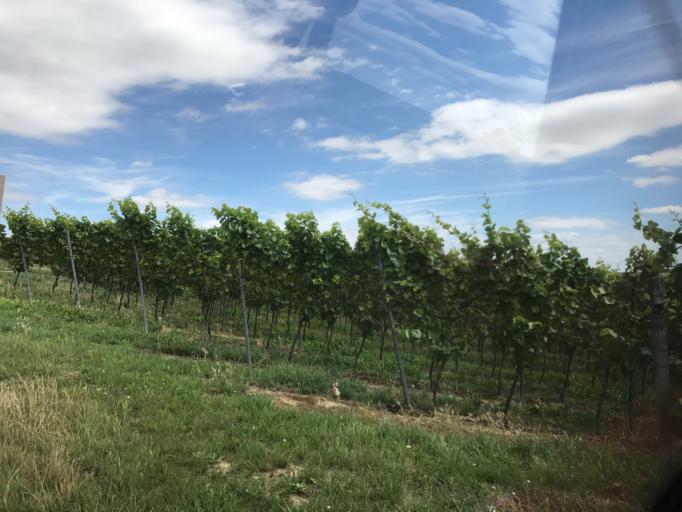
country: DE
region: Rheinland-Pfalz
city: Jugenheim
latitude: 49.9000
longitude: 8.0927
